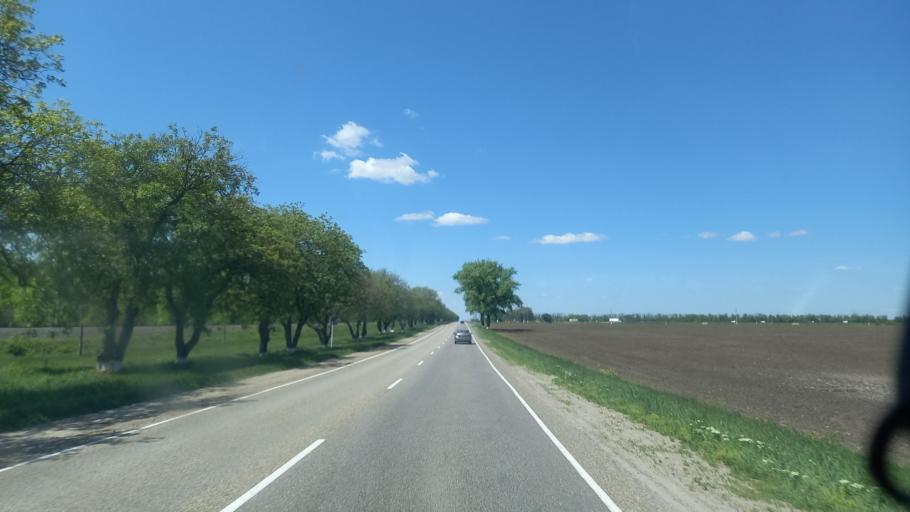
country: RU
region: Krasnodarskiy
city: Tbilisskaya
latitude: 45.3664
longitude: 40.1390
